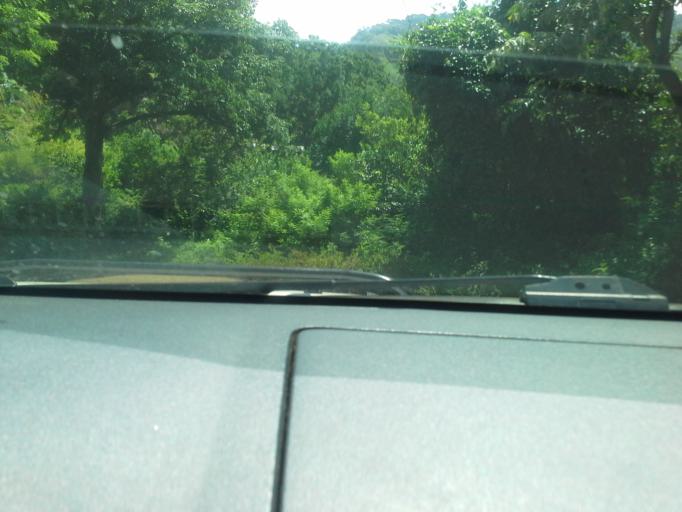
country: NI
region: Matagalpa
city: Terrabona
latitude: 12.7380
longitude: -85.9260
